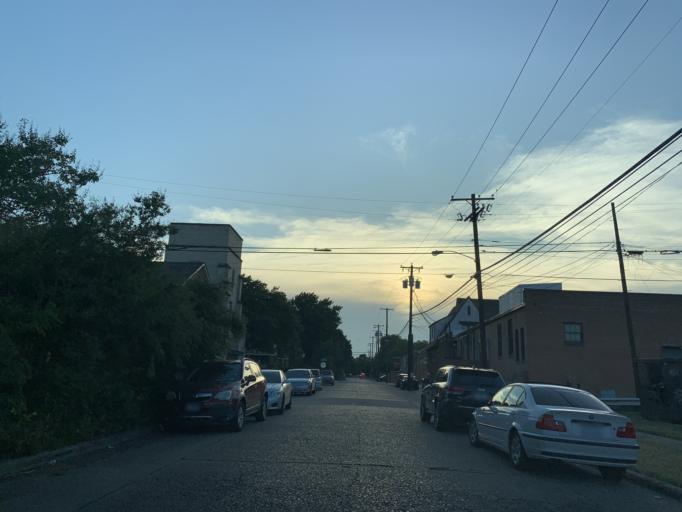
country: US
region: Texas
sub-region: Dallas County
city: Cockrell Hill
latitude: 32.7490
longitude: -96.8431
